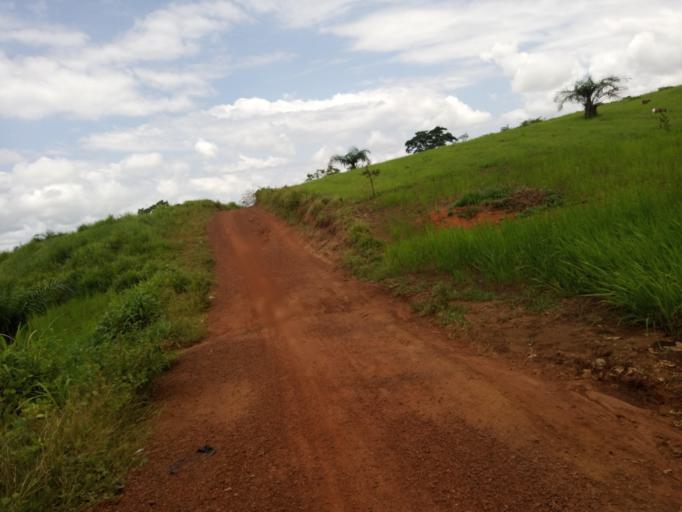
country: SL
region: Northern Province
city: Kamakwie
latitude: 9.4824
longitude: -12.2431
